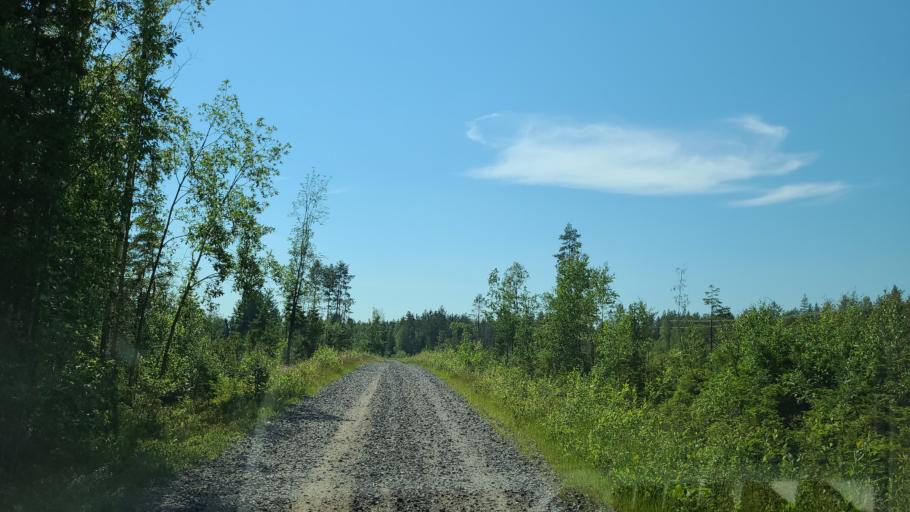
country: SE
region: Vaesterbotten
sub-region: Robertsfors Kommun
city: Robertsfors
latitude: 64.0936
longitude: 20.8353
